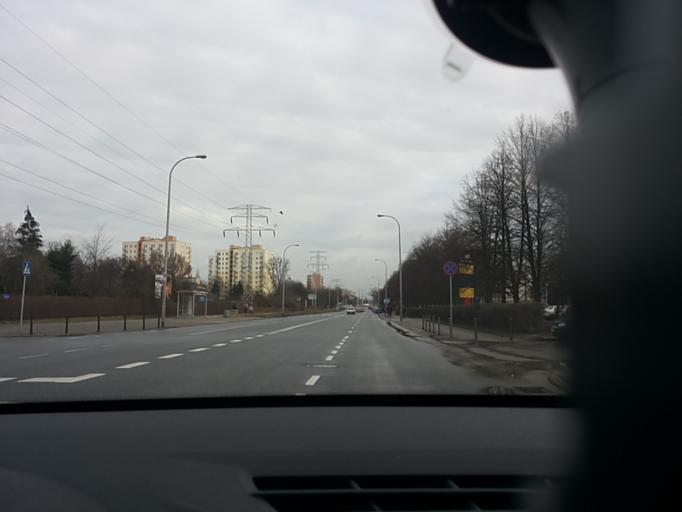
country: PL
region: Masovian Voivodeship
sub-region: Warszawa
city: Ochota
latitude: 52.1888
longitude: 20.9953
